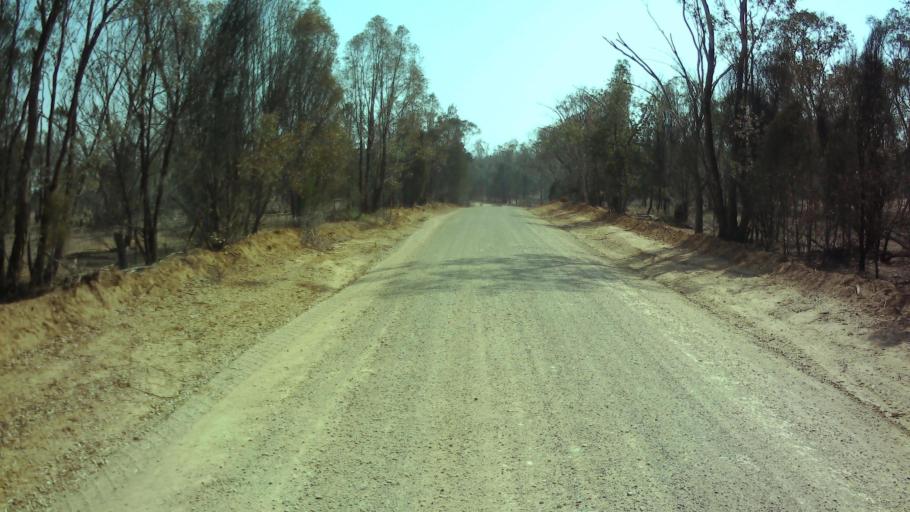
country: AU
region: New South Wales
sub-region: Weddin
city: Grenfell
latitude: -33.6632
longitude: 148.2744
